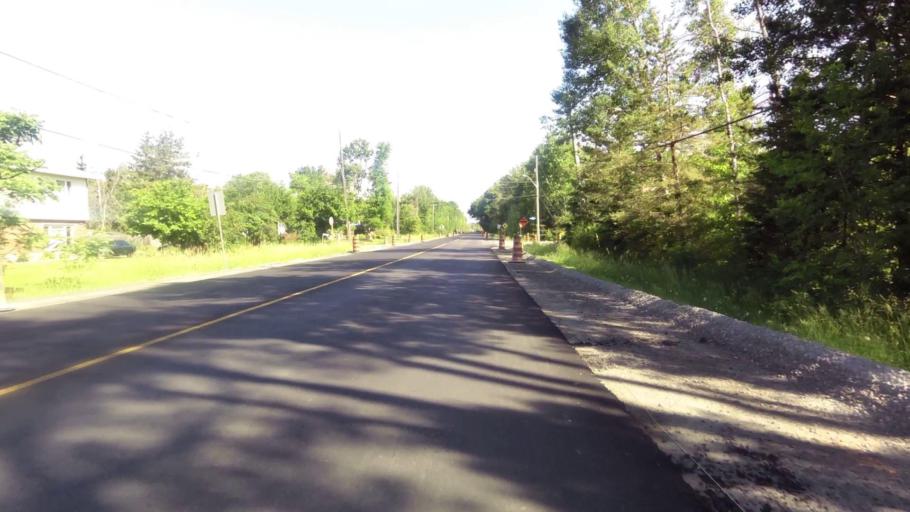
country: CA
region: Ontario
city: Ottawa
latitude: 45.2592
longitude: -75.5956
